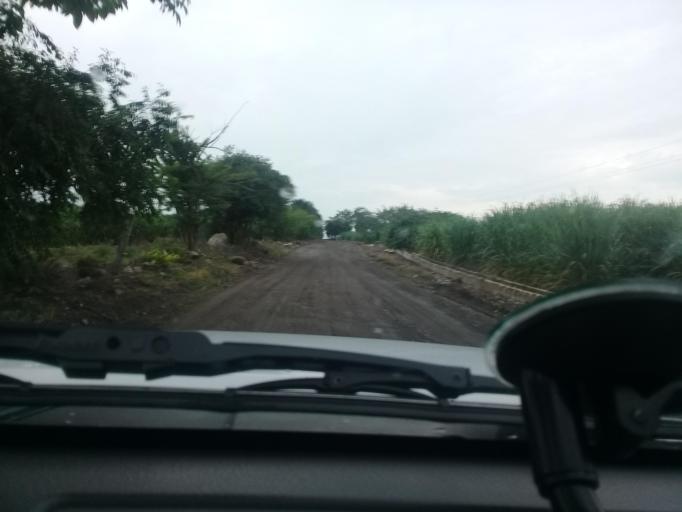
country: MX
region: Veracruz
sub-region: Puente Nacional
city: Cabezas
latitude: 19.3627
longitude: -96.4248
